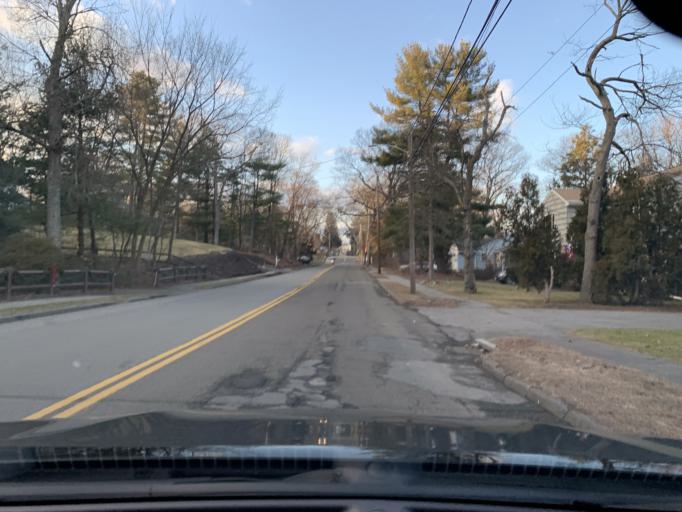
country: US
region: Massachusetts
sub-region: Essex County
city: Lynnfield
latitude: 42.5215
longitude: -71.0182
